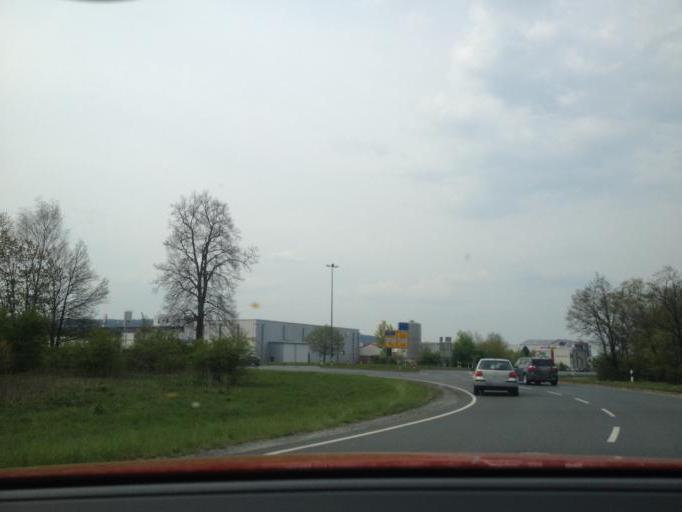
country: DE
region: Bavaria
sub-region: Upper Franconia
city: Bindlach
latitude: 49.9636
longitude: 11.6097
